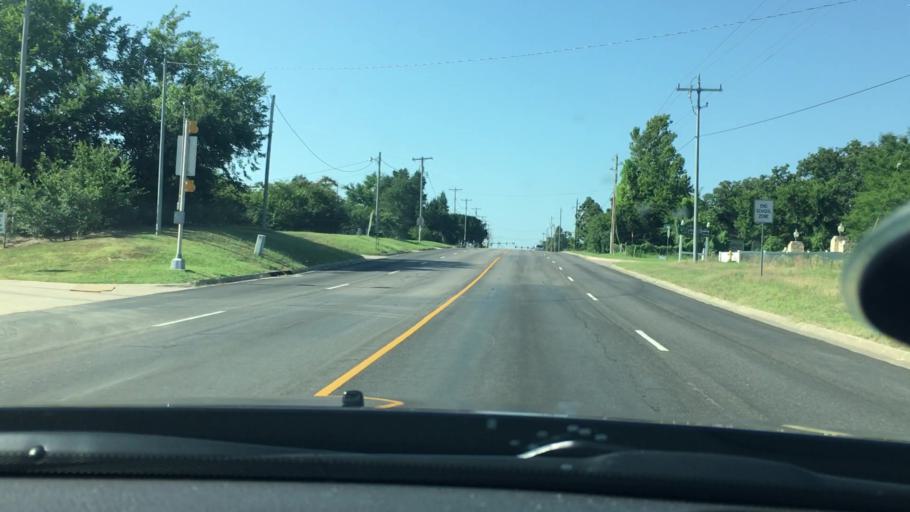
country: US
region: Oklahoma
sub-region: Pontotoc County
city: Ada
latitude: 34.7859
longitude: -96.6349
